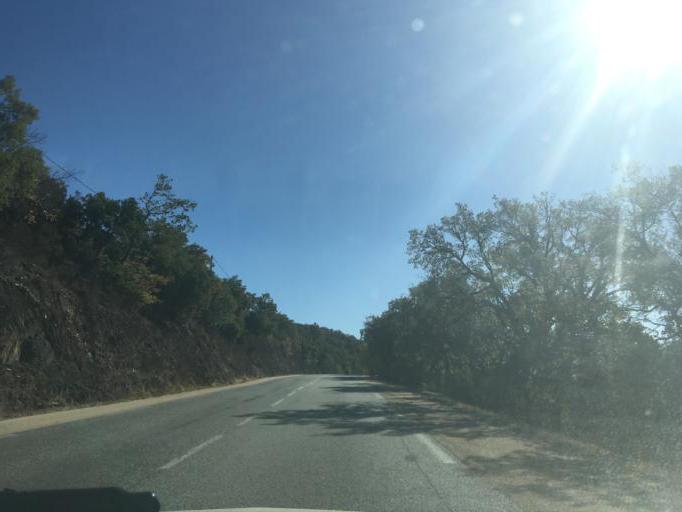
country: FR
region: Provence-Alpes-Cote d'Azur
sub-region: Departement du Var
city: Grimaud
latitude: 43.2845
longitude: 6.5040
